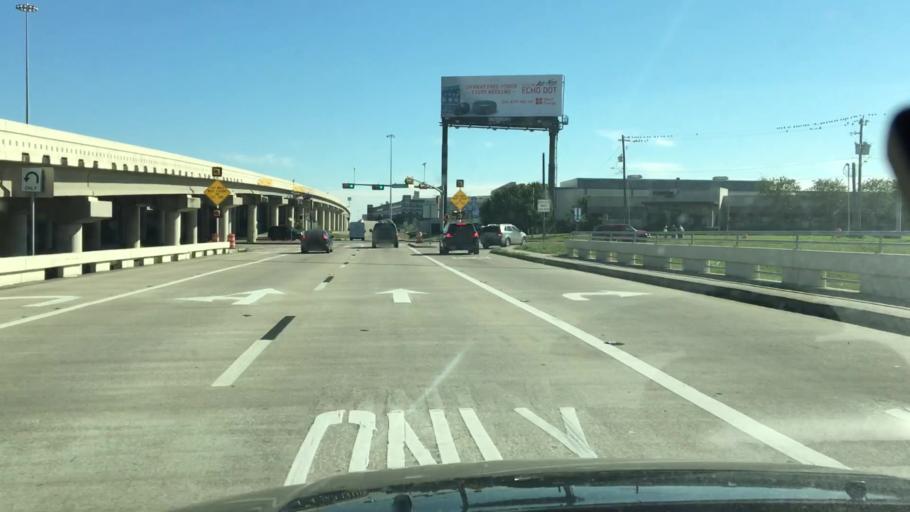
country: US
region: Texas
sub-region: Harris County
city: Houston
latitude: 29.7763
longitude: -95.3900
